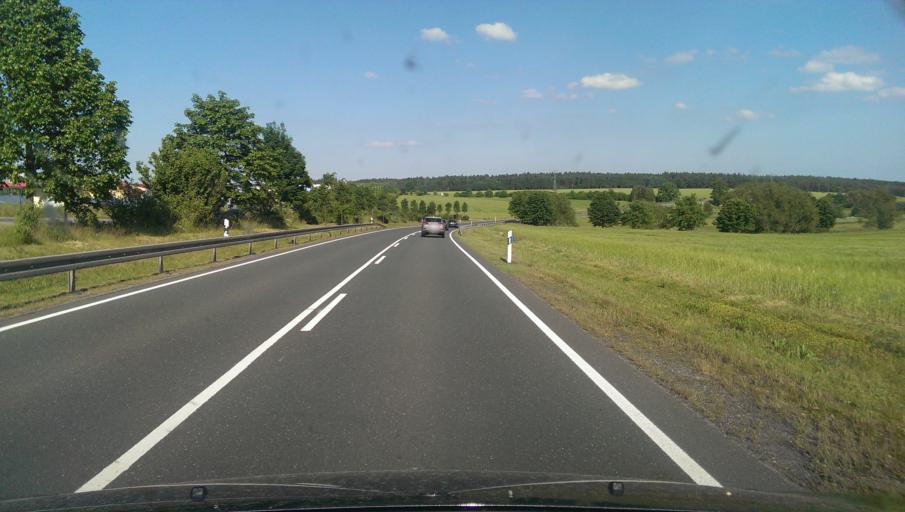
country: DE
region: Thuringia
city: Lederhose
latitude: 50.8051
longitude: 11.9163
